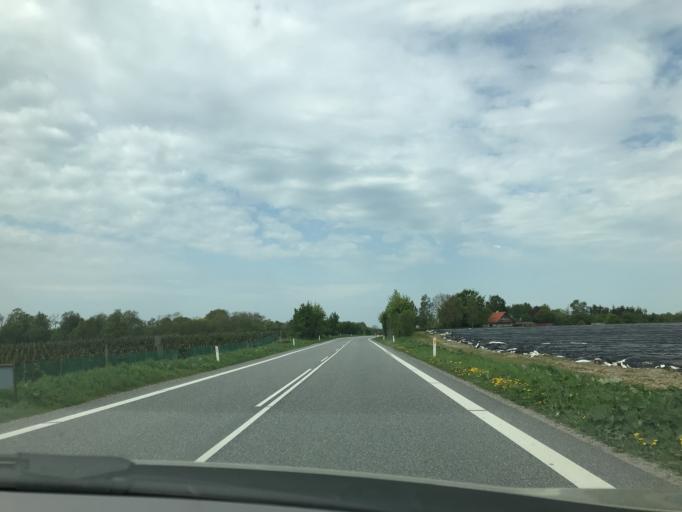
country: DK
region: South Denmark
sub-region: Assens Kommune
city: Assens
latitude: 55.3117
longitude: 9.9427
